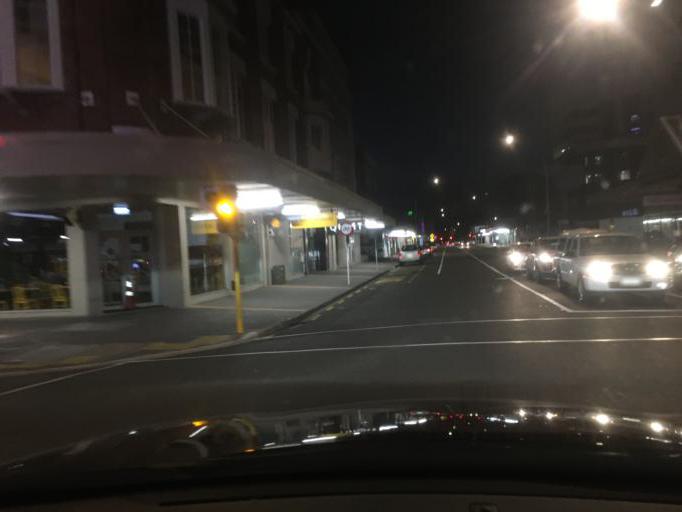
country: NZ
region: Waikato
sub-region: Hamilton City
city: Hamilton
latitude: -37.7833
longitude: 175.2793
